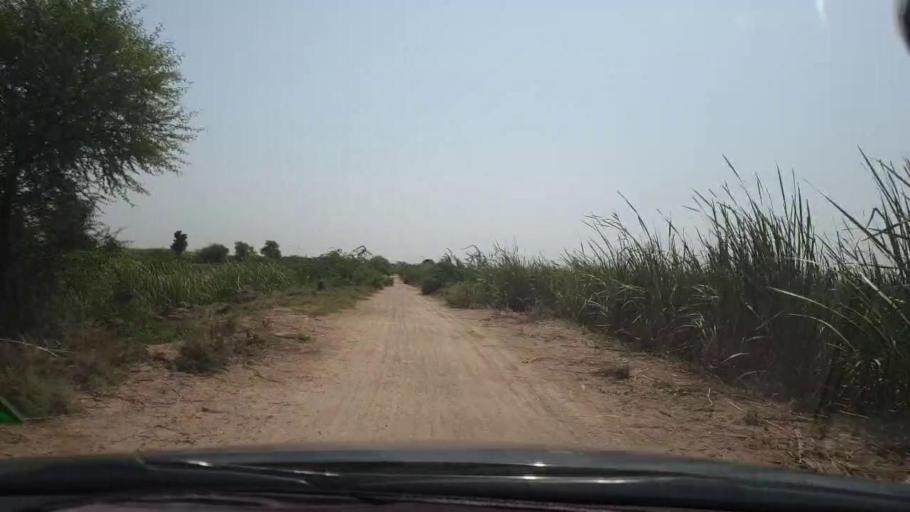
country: PK
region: Sindh
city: Tando Bago
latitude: 24.7893
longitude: 69.1172
